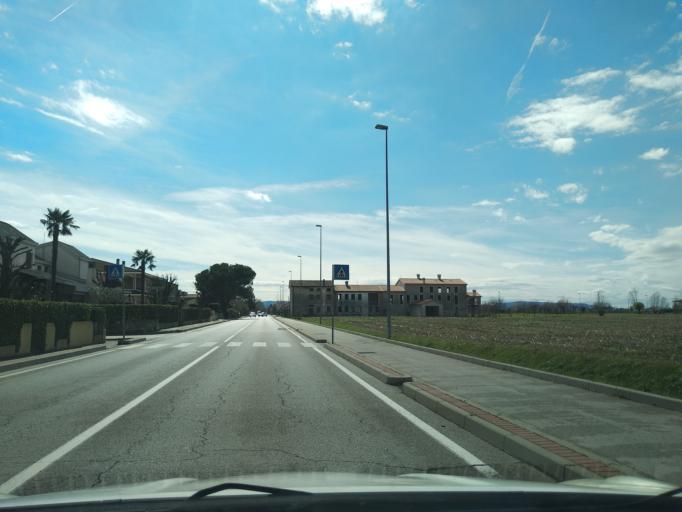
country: IT
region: Veneto
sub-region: Provincia di Vicenza
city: Monticello Conte Otto
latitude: 45.5925
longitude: 11.5799
